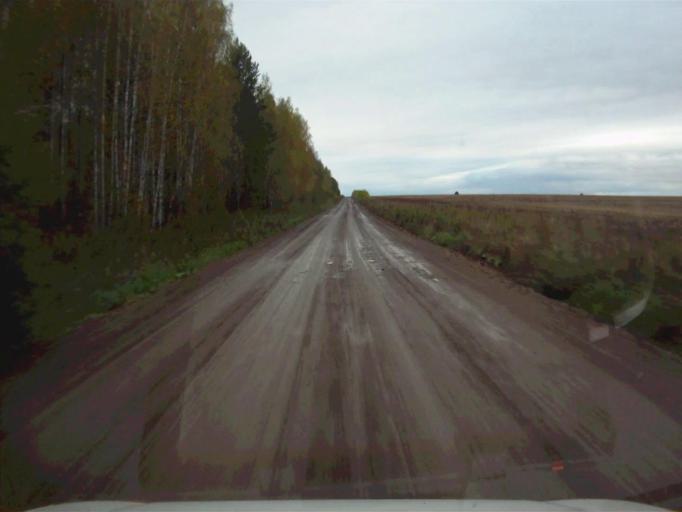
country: RU
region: Sverdlovsk
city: Mikhaylovsk
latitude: 56.1514
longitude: 59.2679
